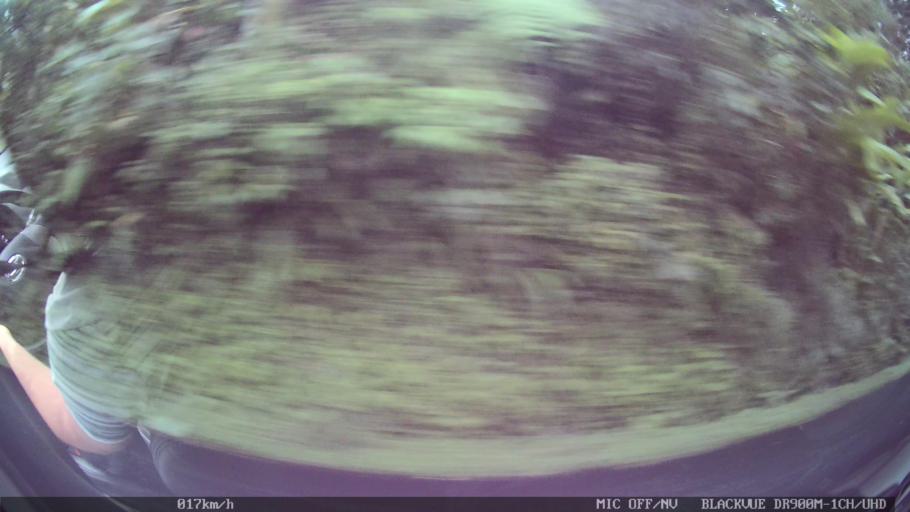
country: ID
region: Bali
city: Peneng
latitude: -8.3622
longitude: 115.1791
